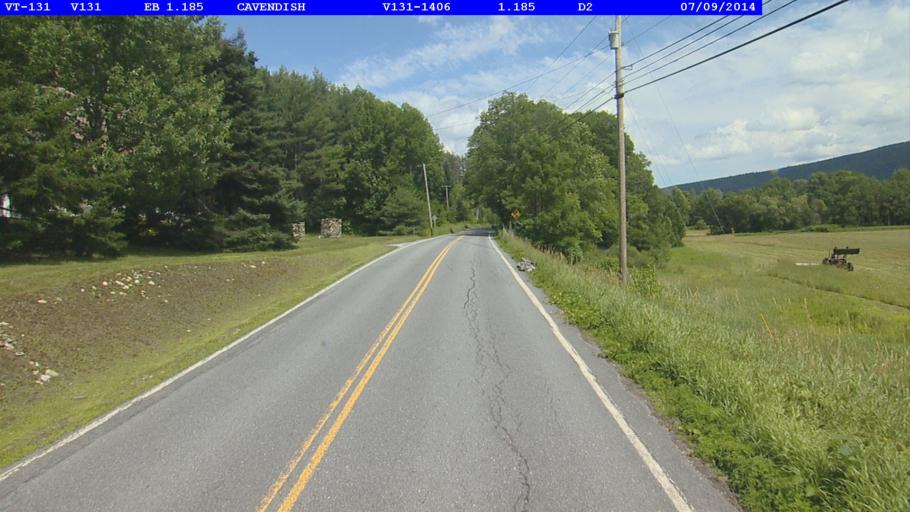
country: US
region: Vermont
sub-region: Windsor County
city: Chester
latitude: 43.3850
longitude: -72.6252
